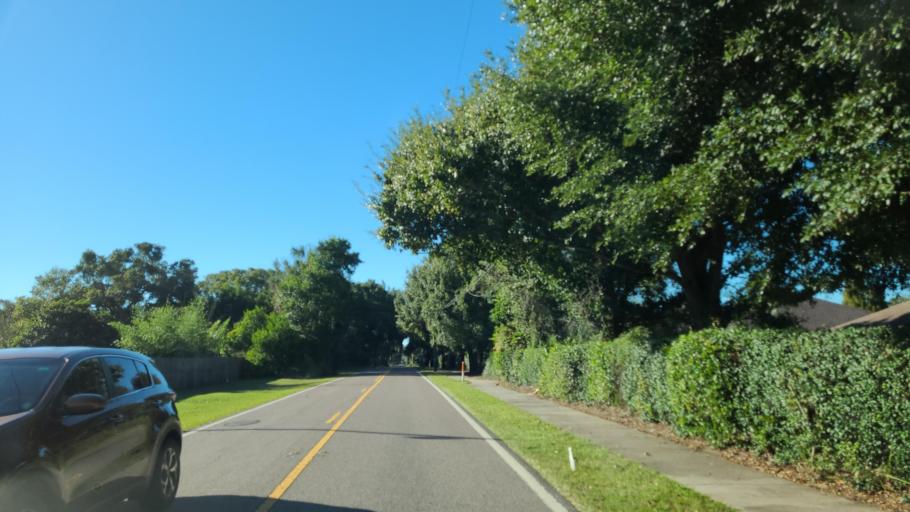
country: US
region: Florida
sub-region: Hillsborough County
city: Valrico
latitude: 27.9183
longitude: -82.2590
